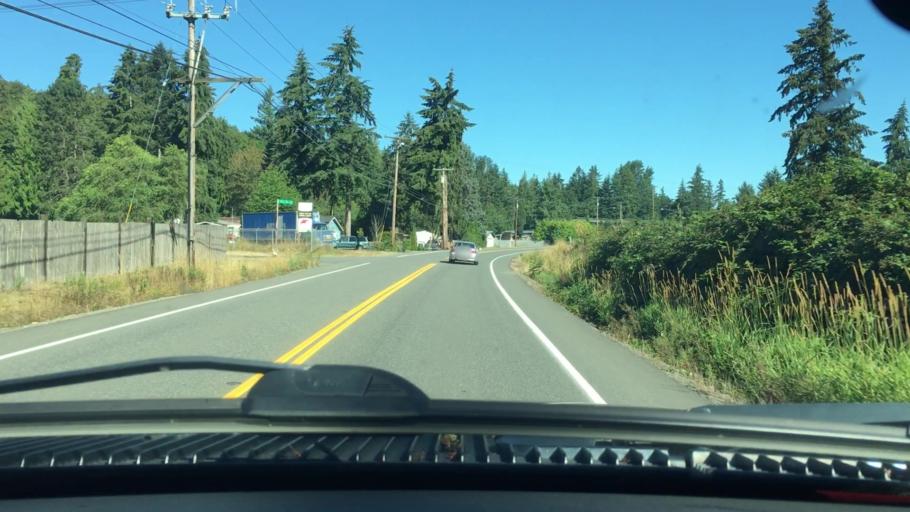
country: US
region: Washington
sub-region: King County
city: Covington
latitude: 47.3451
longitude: -122.1364
